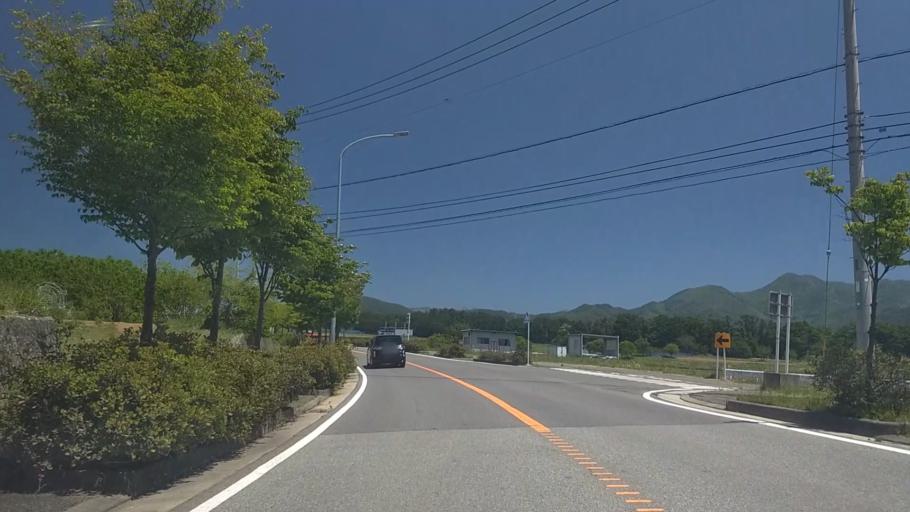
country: JP
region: Yamanashi
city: Nirasaki
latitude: 35.8406
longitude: 138.4329
